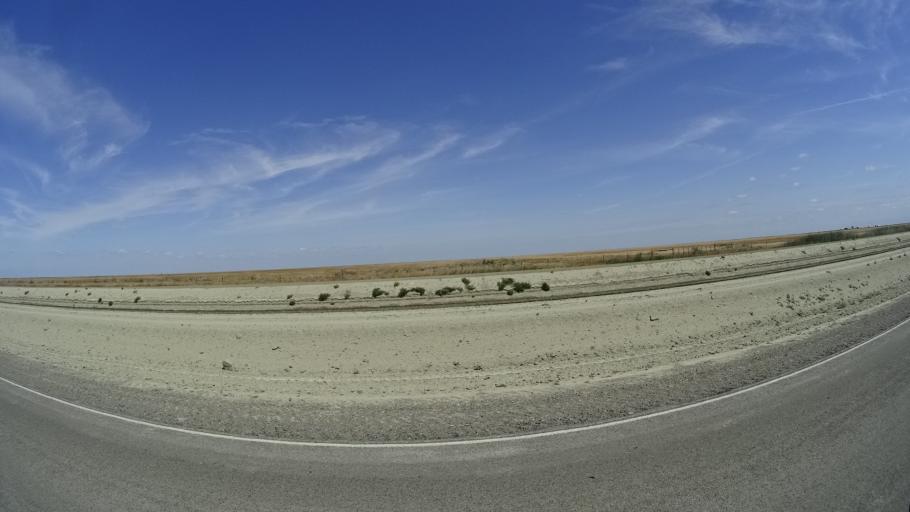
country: US
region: California
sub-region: Tulare County
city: Alpaugh
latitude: 35.9345
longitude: -119.6186
